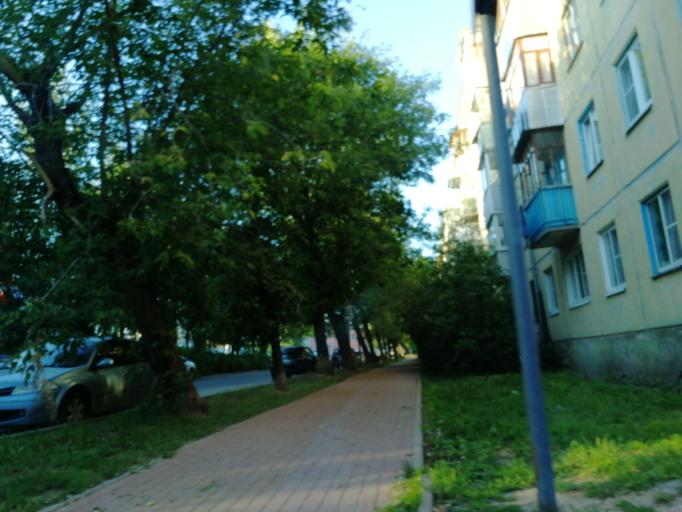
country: RU
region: Kaluga
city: Kaluga
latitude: 54.5193
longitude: 36.2877
